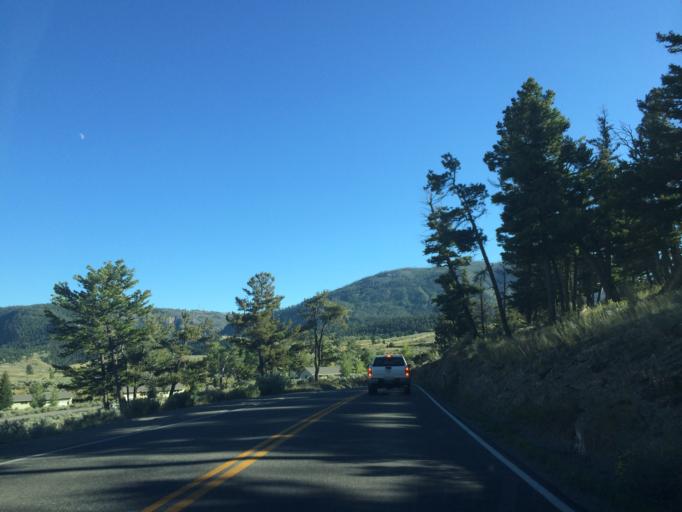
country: US
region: Montana
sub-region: Gallatin County
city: West Yellowstone
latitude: 44.9730
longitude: -110.6946
